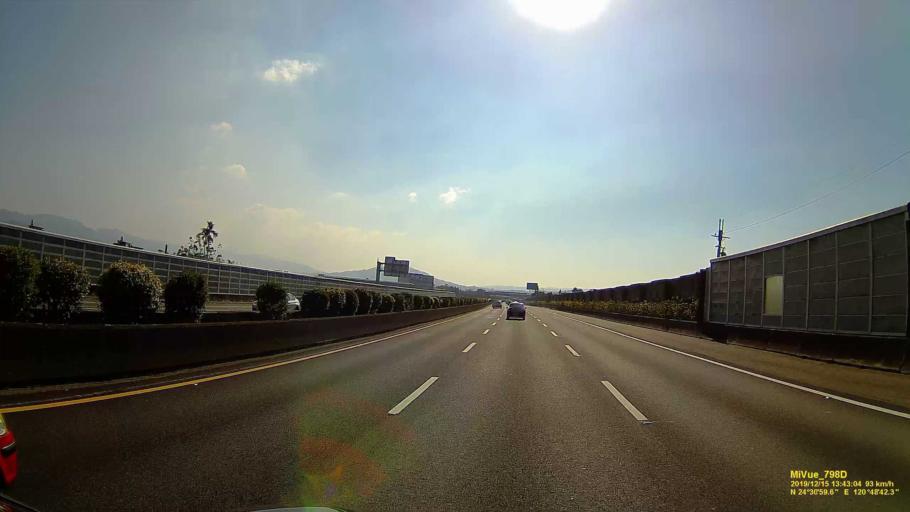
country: TW
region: Taiwan
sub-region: Miaoli
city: Miaoli
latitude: 24.5161
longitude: 120.8116
